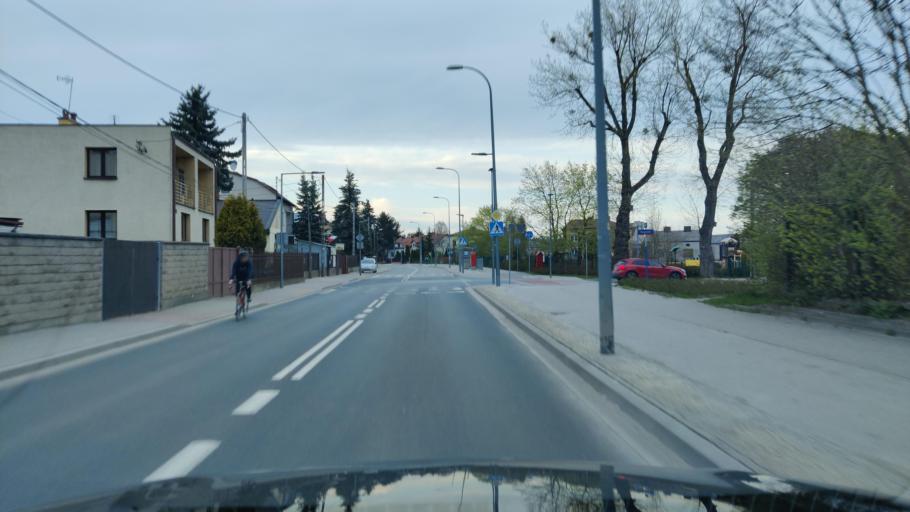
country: PL
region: Masovian Voivodeship
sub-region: Warszawa
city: Kabaty
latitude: 52.1274
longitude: 21.1036
